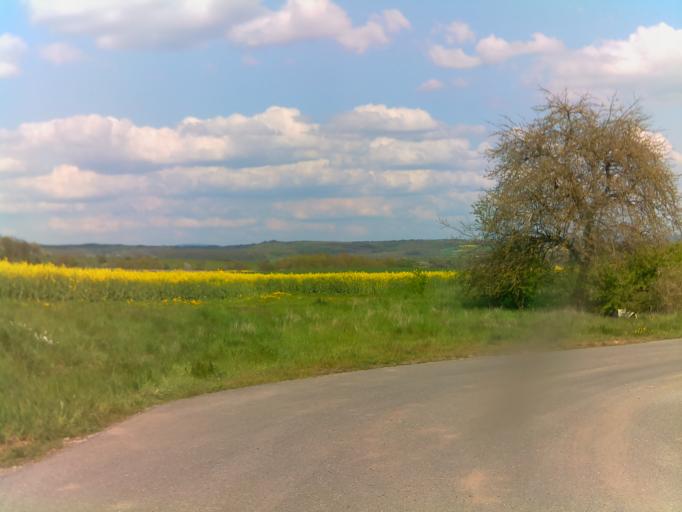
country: DE
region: Thuringia
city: Westhausen
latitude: 50.3512
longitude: 10.7182
